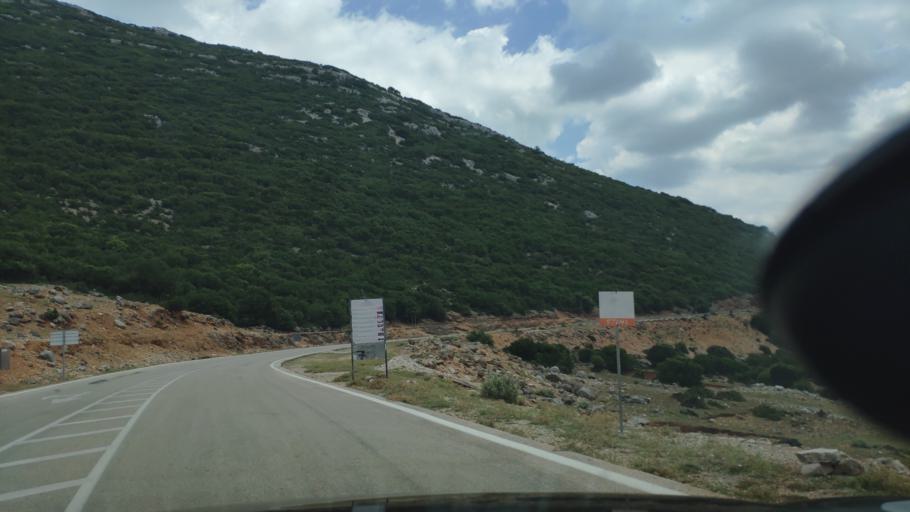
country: GR
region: Epirus
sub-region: Nomos Artas
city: Kampi
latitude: 39.2753
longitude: 20.9652
